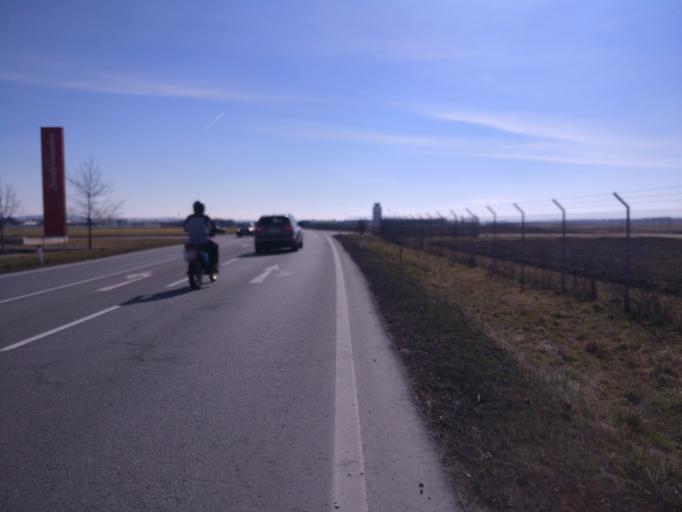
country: AT
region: Styria
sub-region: Politischer Bezirk Graz-Umgebung
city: Feldkirchen bei Graz
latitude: 47.0047
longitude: 15.4411
